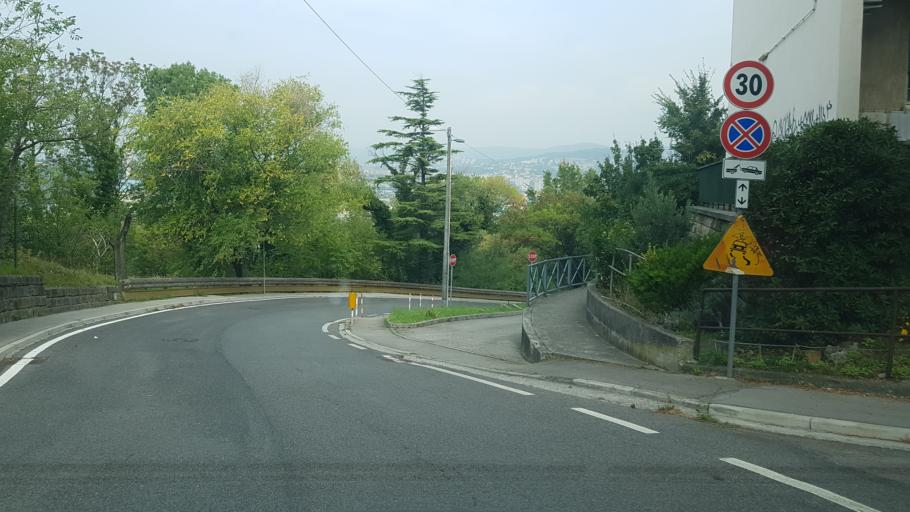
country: IT
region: Friuli Venezia Giulia
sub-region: Provincia di Trieste
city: Domio
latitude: 45.6013
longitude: 13.8054
